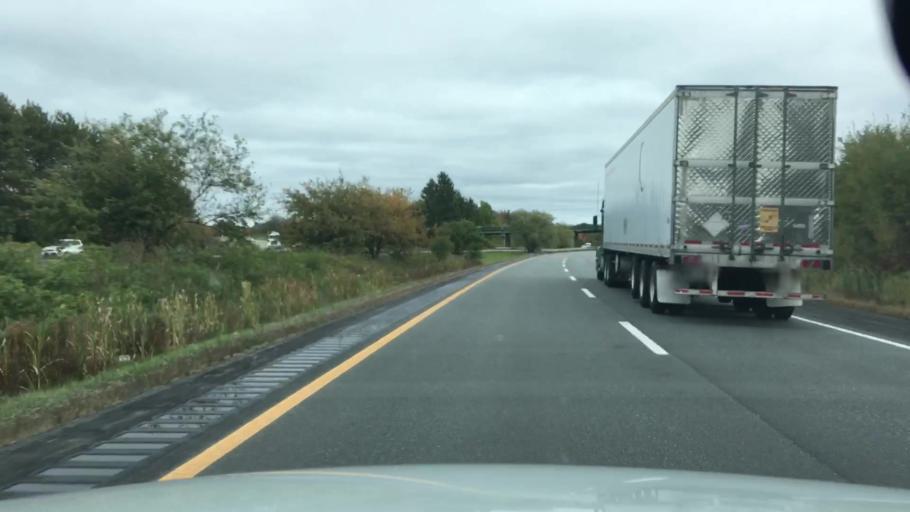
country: US
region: Maine
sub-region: Penobscot County
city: Newport
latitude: 44.8349
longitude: -69.2950
